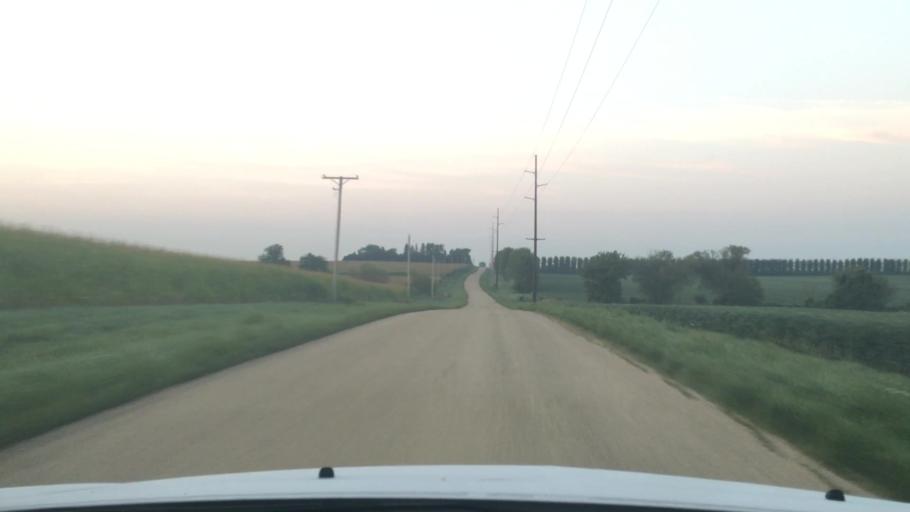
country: US
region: Illinois
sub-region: Ogle County
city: Rochelle
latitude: 41.8799
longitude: -89.0010
